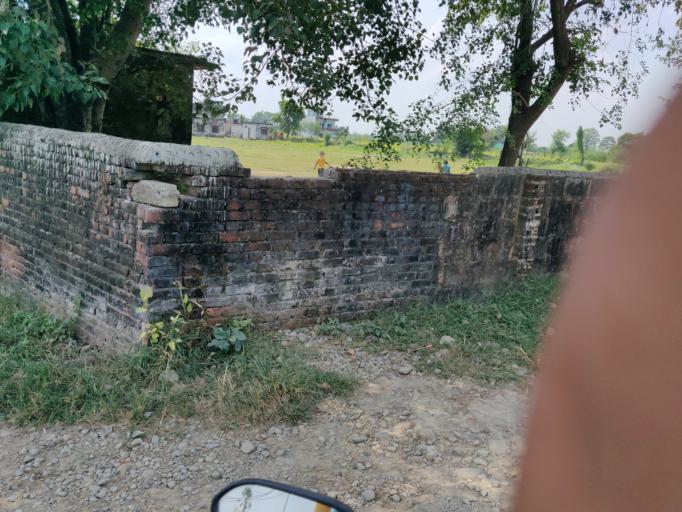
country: NP
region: Western Region
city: Butwal
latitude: 27.6078
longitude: 83.4842
